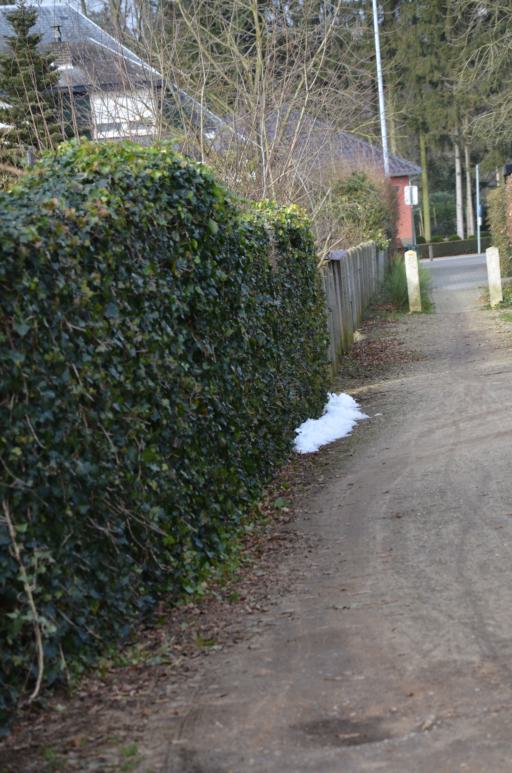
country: BE
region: Flanders
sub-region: Provincie Antwerpen
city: Lille
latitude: 51.2224
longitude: 4.8325
